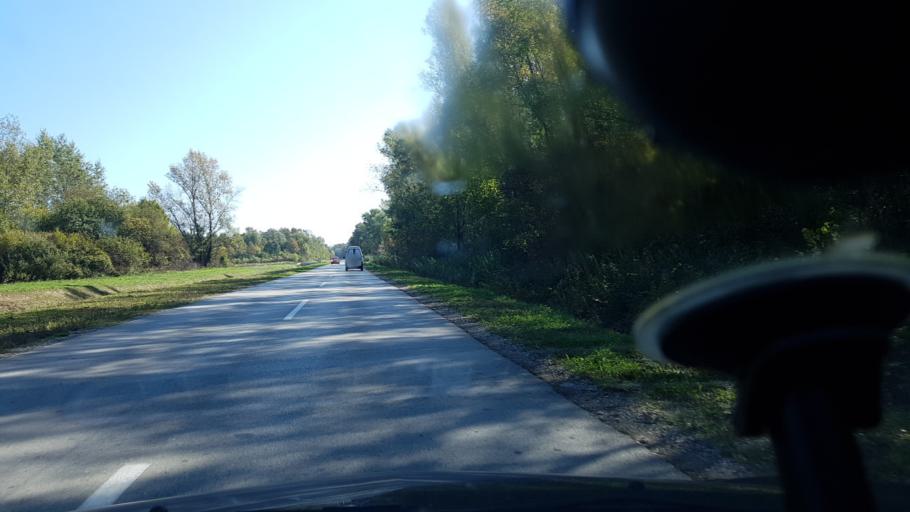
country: HR
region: Zagrebacka
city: Brckovljani
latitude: 45.7650
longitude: 16.2397
